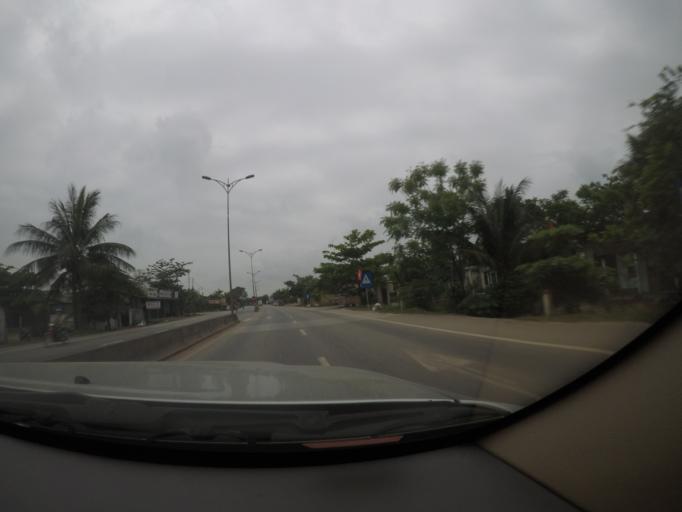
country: VN
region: Thua Thien-Hue
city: Phong Dien
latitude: 16.6041
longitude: 107.3260
